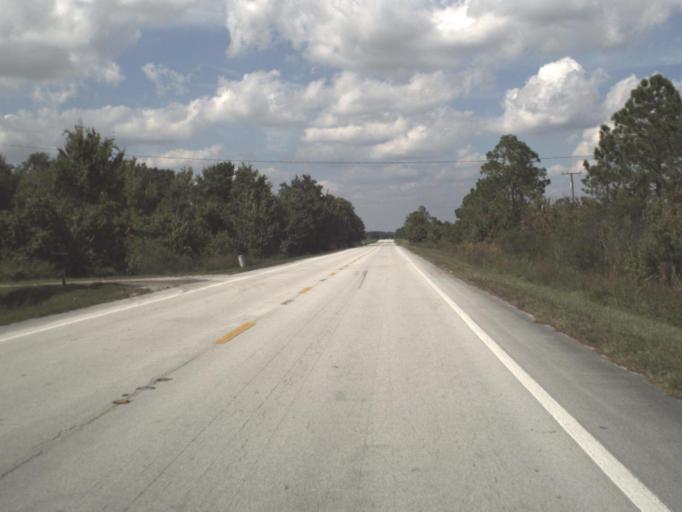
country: US
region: Florida
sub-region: Okeechobee County
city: Cypress Quarters
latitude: 27.5525
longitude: -80.8200
